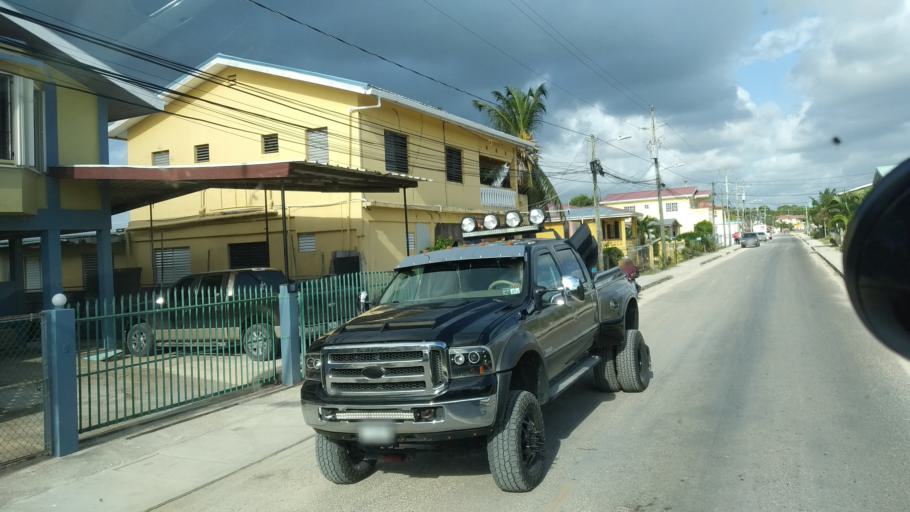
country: BZ
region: Belize
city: Belize City
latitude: 17.5120
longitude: -88.2257
